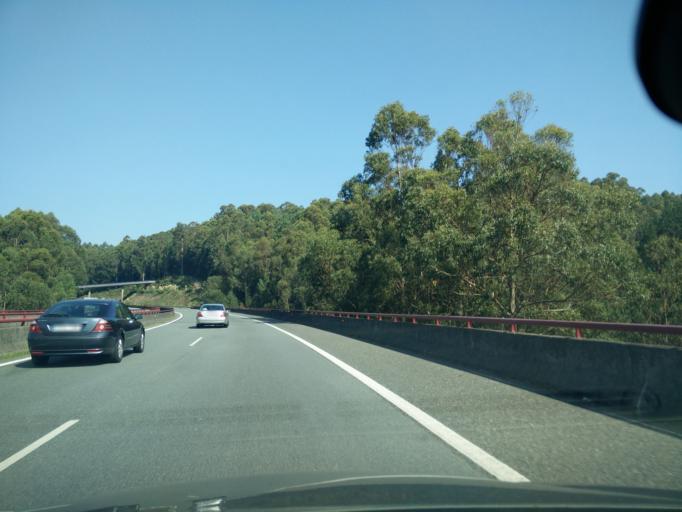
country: ES
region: Galicia
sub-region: Provincia da Coruna
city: Mino
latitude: 43.3350
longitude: -8.1974
